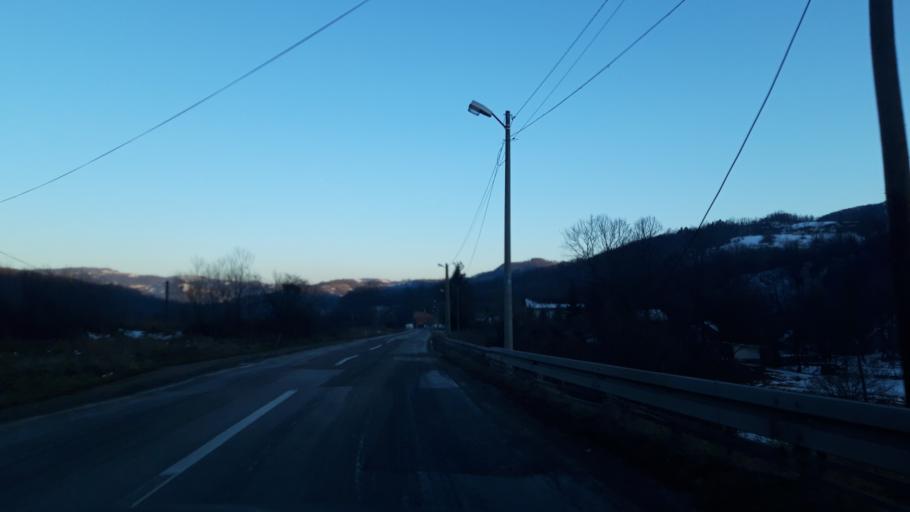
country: BA
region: Republika Srpska
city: Milici
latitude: 44.1645
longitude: 19.0443
